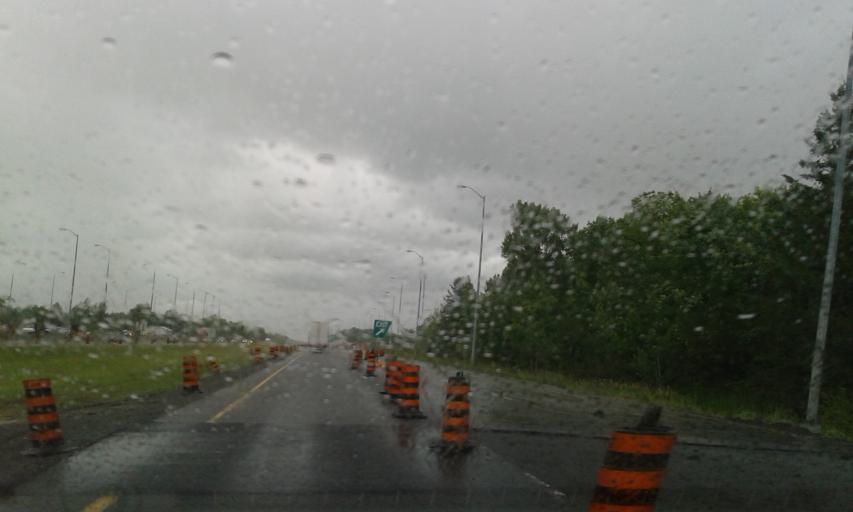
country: CA
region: Ontario
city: Gananoque
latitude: 44.3581
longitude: -76.0874
